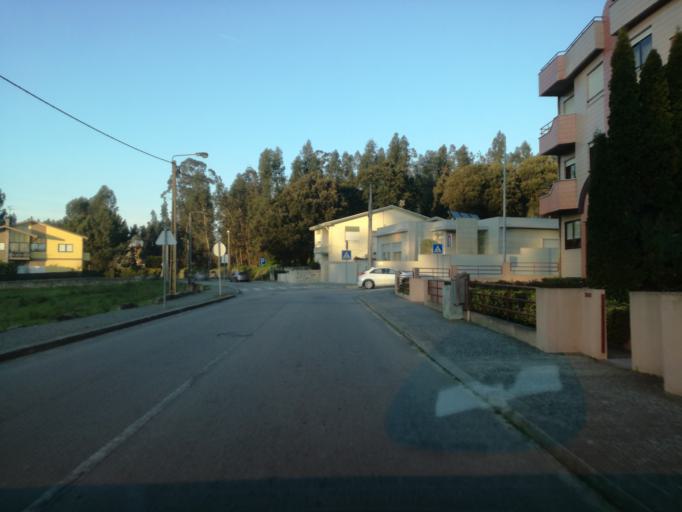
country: PT
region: Porto
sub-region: Maia
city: Milheiros
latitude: 41.2215
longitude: -8.5904
